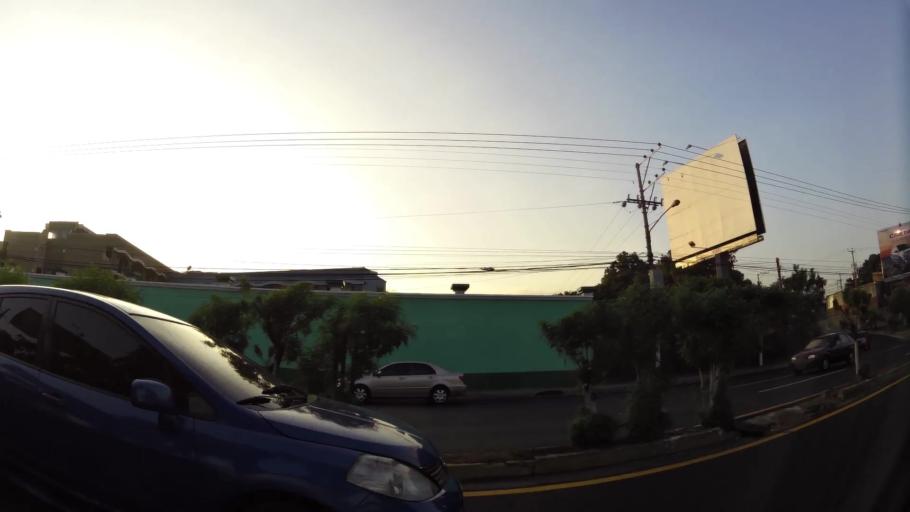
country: SV
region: San Salvador
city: San Salvador
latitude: 13.6903
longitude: -89.2173
